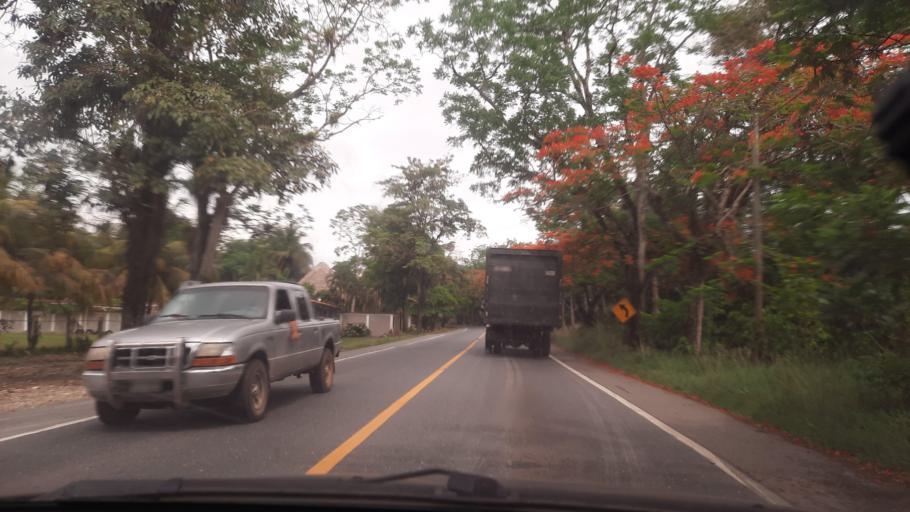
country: GT
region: Izabal
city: Morales
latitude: 15.4641
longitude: -88.9162
